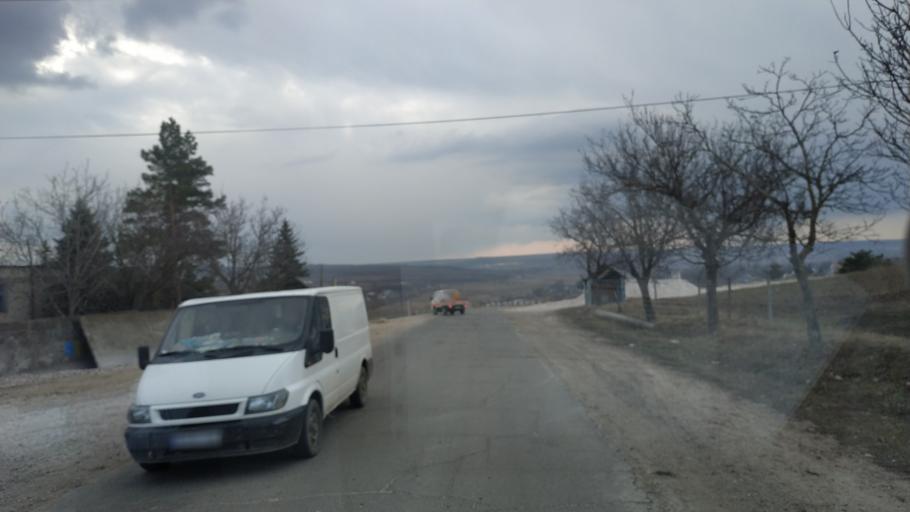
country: MD
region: Anenii Noi
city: Anenii Noi
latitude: 46.8952
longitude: 29.3049
